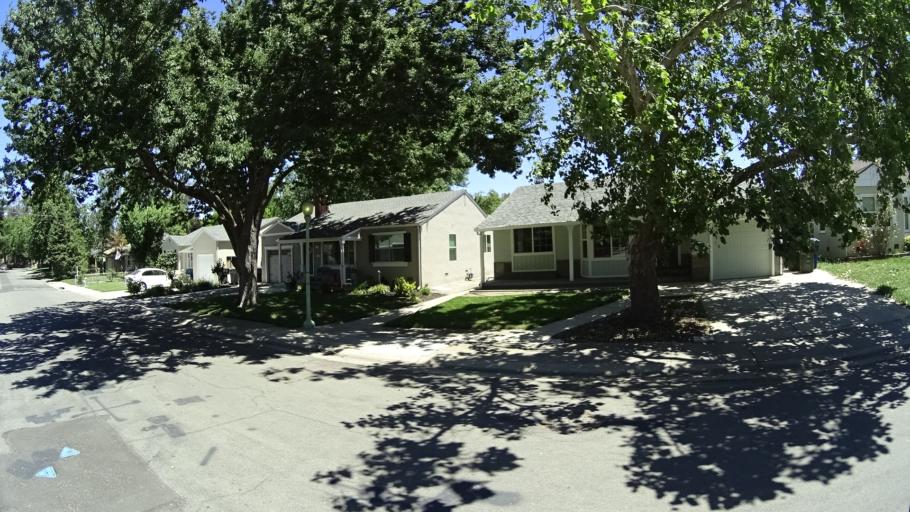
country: US
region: California
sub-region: Sacramento County
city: Sacramento
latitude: 38.5763
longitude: -121.4372
